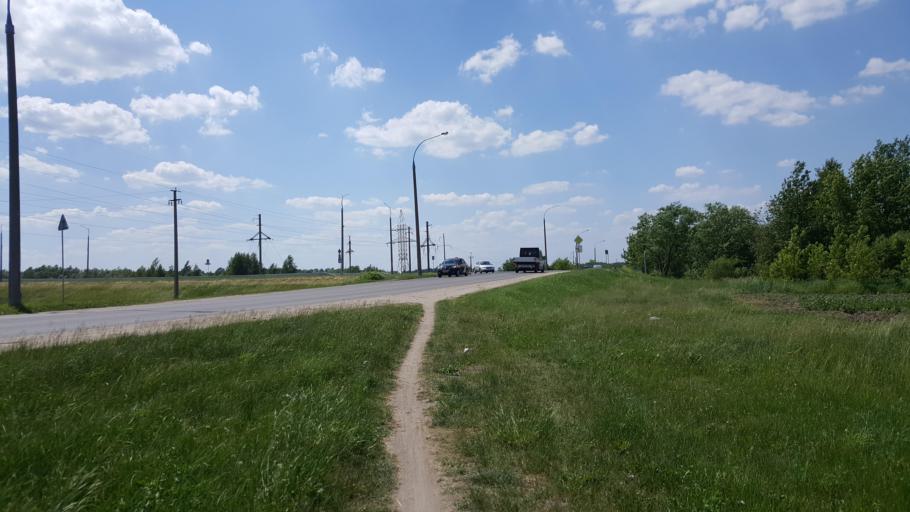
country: BY
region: Brest
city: Kobryn
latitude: 52.2186
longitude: 24.3329
